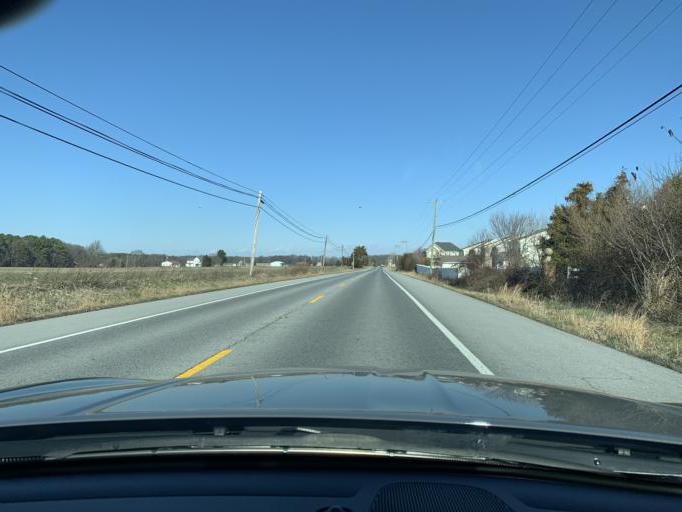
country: US
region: Maryland
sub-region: Queen Anne's County
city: Centreville
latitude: 39.0630
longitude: -76.0516
